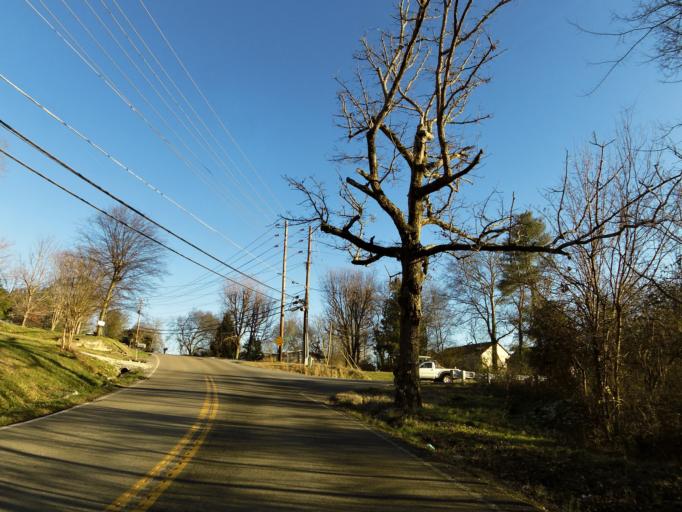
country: US
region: Tennessee
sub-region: Knox County
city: Farragut
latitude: 35.8800
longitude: -84.1276
